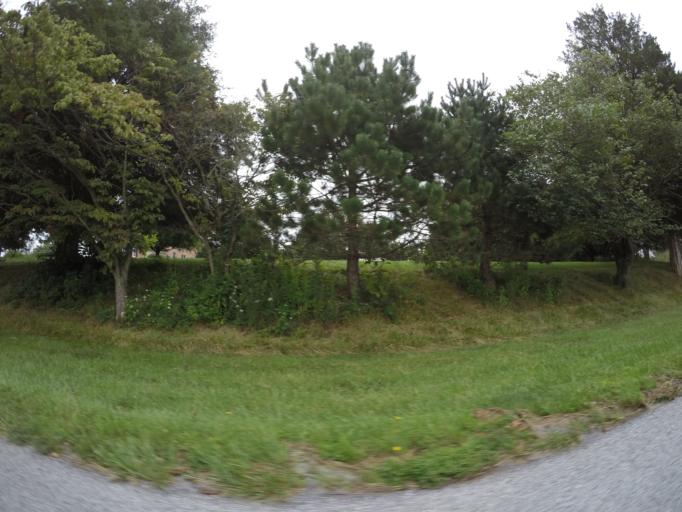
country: US
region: Maryland
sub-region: Carroll County
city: Sykesville
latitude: 39.3388
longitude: -77.0486
